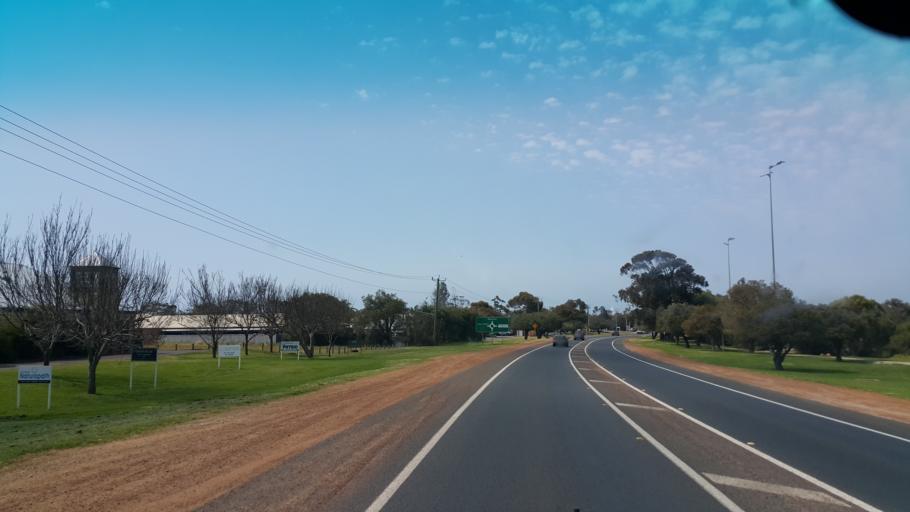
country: AU
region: Western Australia
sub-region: Busselton
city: Dunsborough
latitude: -33.6173
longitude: 115.1038
